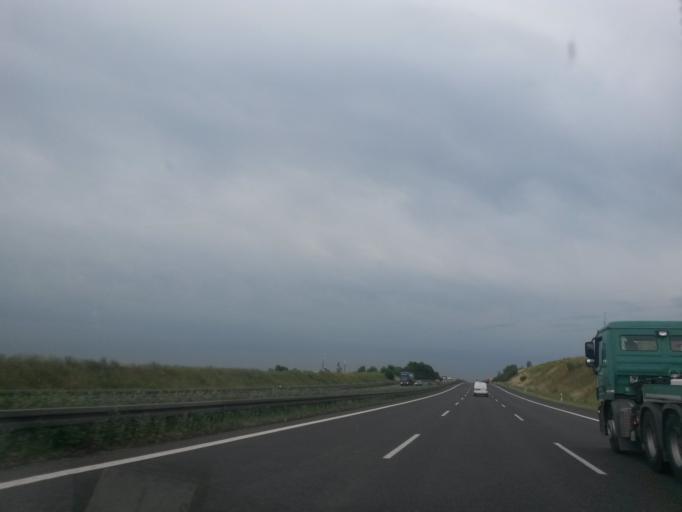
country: DE
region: Bavaria
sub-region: Upper Bavaria
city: Stammham
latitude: 48.8639
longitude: 11.4663
